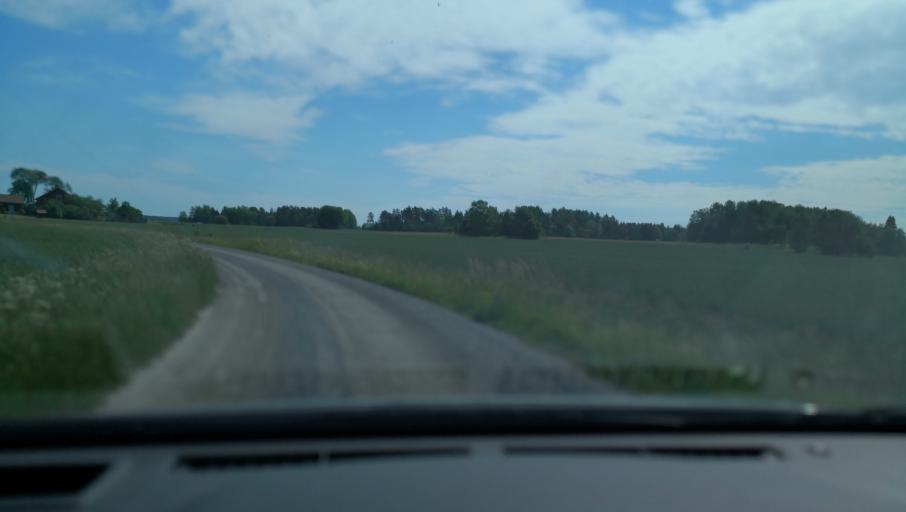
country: SE
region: Uppsala
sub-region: Enkopings Kommun
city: Enkoping
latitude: 59.7017
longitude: 17.1247
